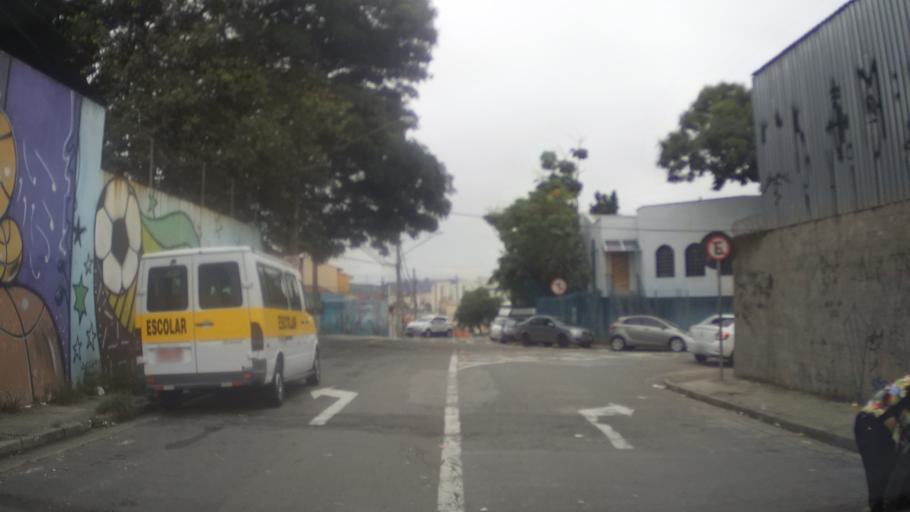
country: BR
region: Sao Paulo
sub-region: Guarulhos
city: Guarulhos
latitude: -23.4511
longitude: -46.5421
